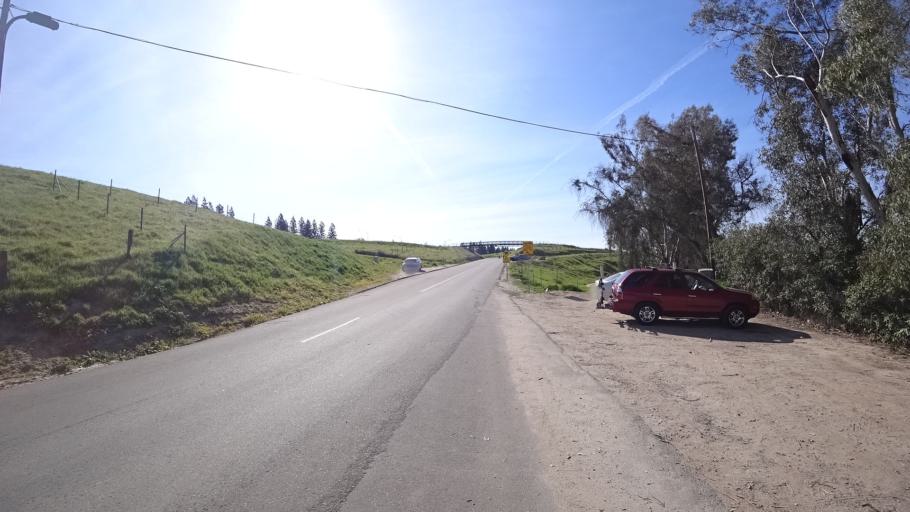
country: US
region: California
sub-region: Fresno County
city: Clovis
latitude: 36.8861
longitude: -119.7787
